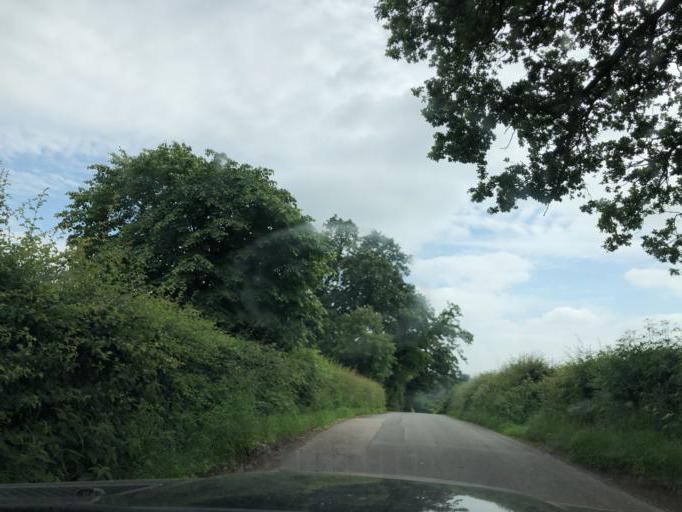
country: GB
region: England
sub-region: Warwickshire
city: Wroxall
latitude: 52.3346
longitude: -1.6415
